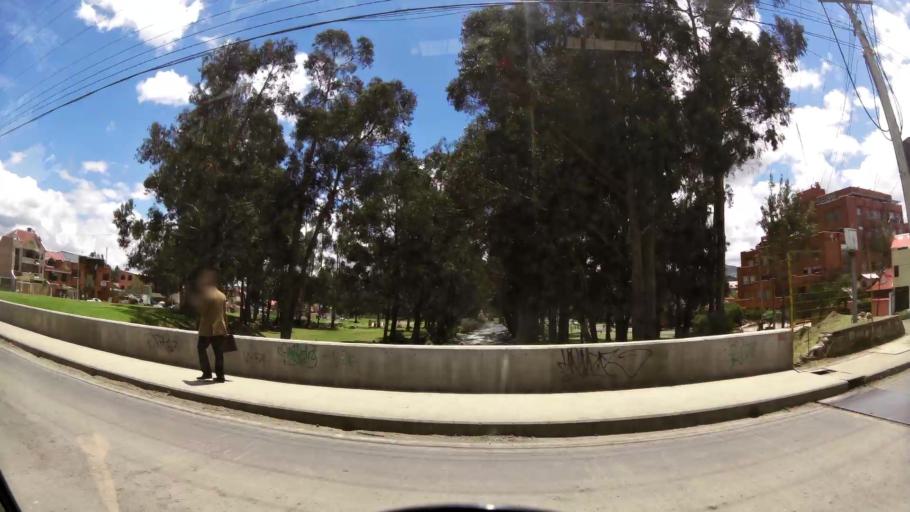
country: EC
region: Azuay
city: Cuenca
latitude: -2.9067
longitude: -79.0333
